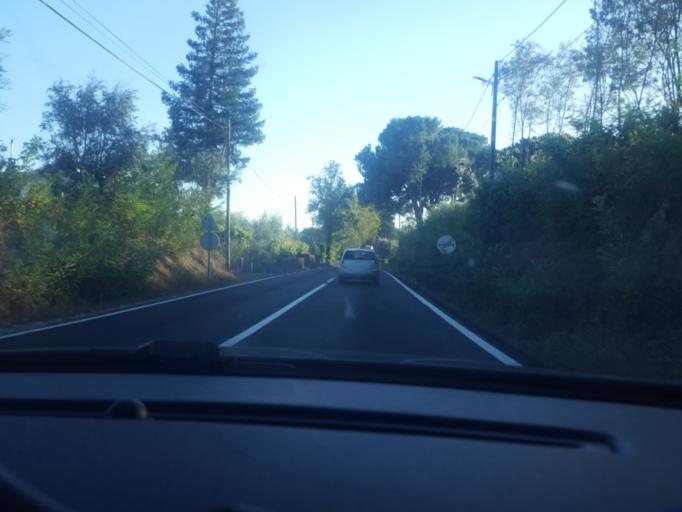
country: PT
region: Viseu
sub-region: Mangualde
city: Mangualde
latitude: 40.5887
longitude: -7.8018
